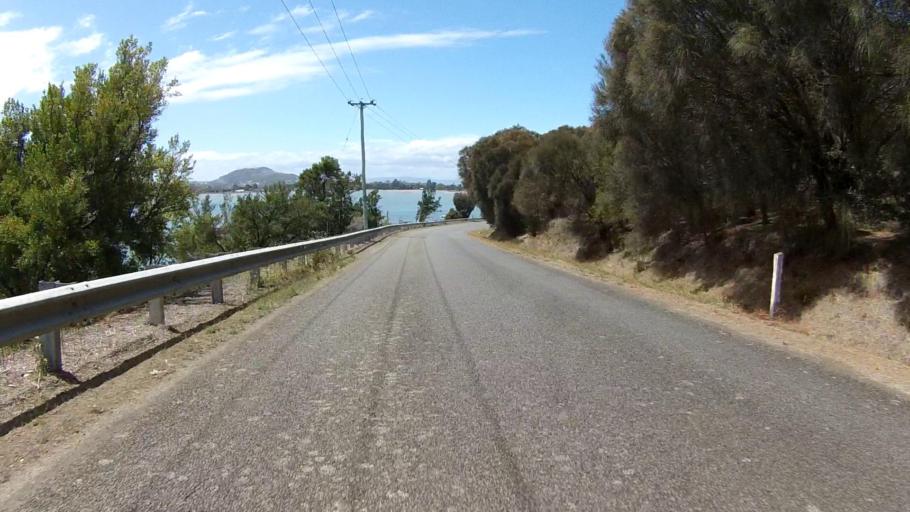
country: AU
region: Tasmania
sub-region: Clarence
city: Lauderdale
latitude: -42.9196
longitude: 147.4736
